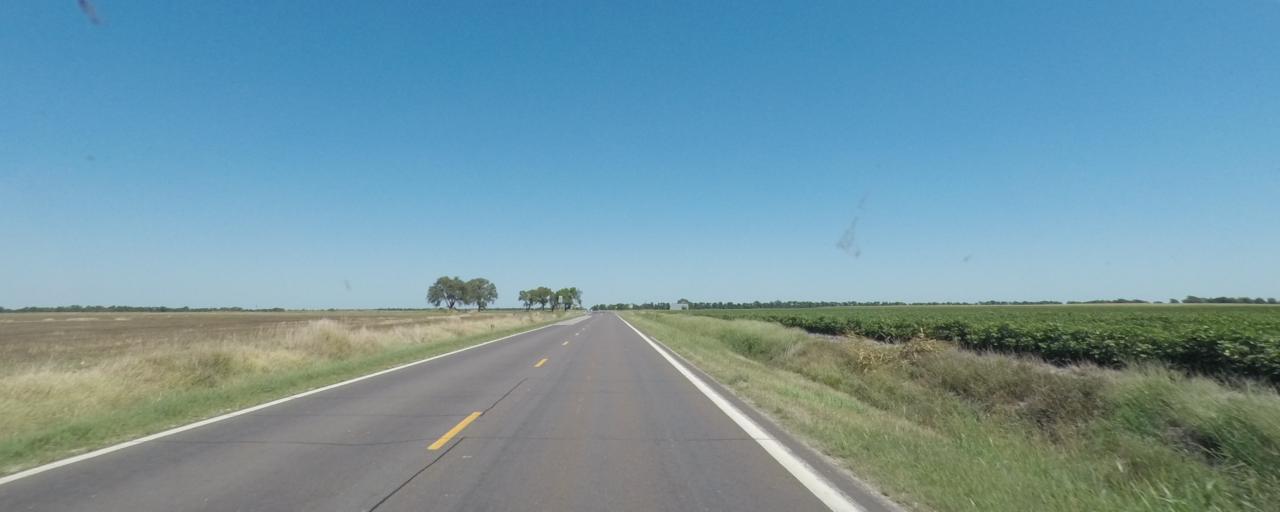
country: US
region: Kansas
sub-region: Sumner County
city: Wellington
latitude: 37.1704
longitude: -97.4020
